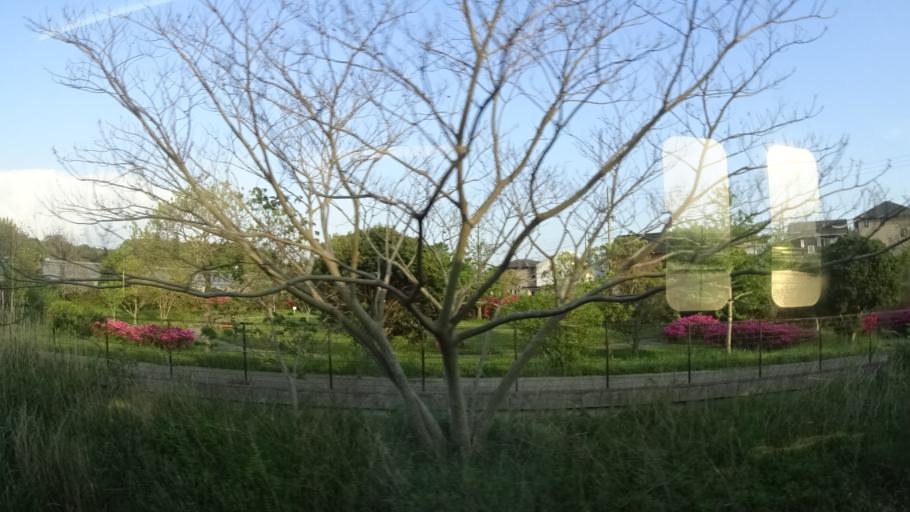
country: JP
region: Aichi
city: Tahara
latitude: 34.6779
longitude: 137.3193
